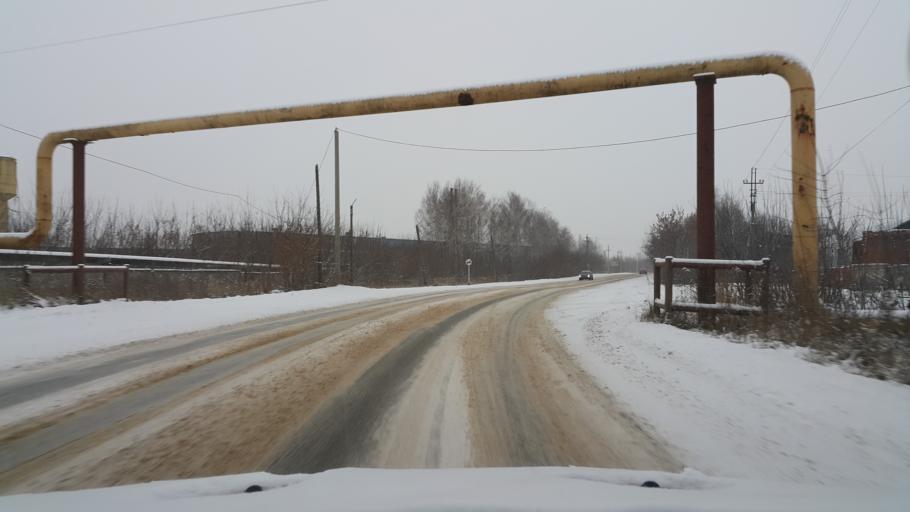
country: RU
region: Tambov
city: Pokrovo-Prigorodnoye
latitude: 52.6586
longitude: 41.4234
